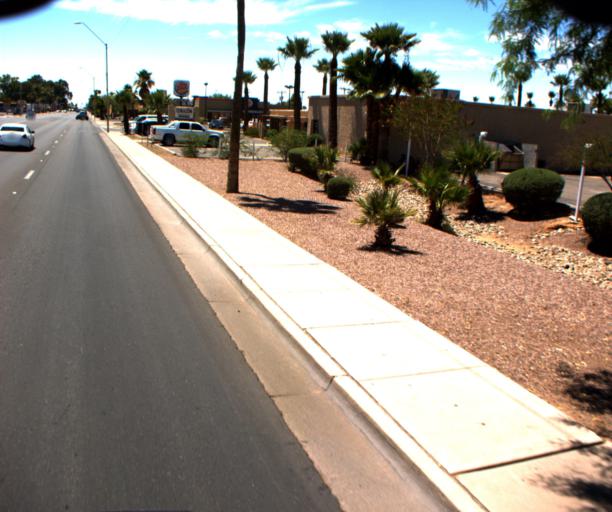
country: US
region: Arizona
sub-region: Pinal County
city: Casa Grande
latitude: 32.8796
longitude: -111.7423
